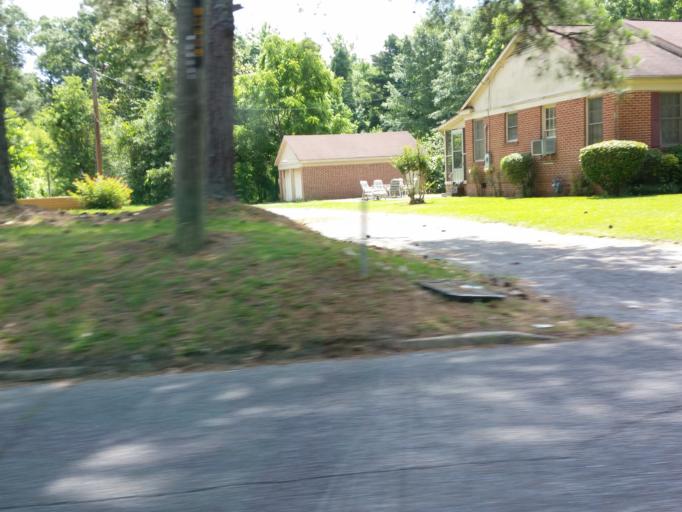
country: US
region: Mississippi
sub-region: Lauderdale County
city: Meridian
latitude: 32.3870
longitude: -88.7168
